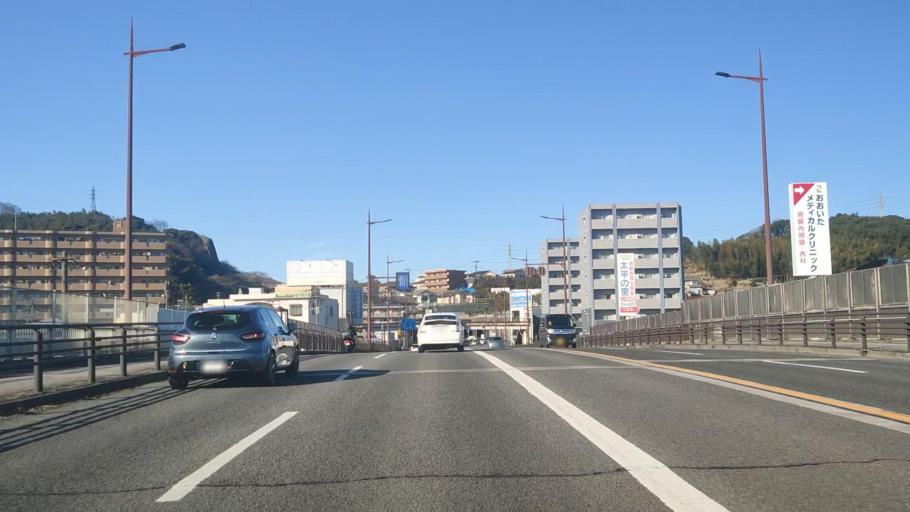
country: JP
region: Oita
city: Oita
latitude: 33.2168
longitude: 131.5954
